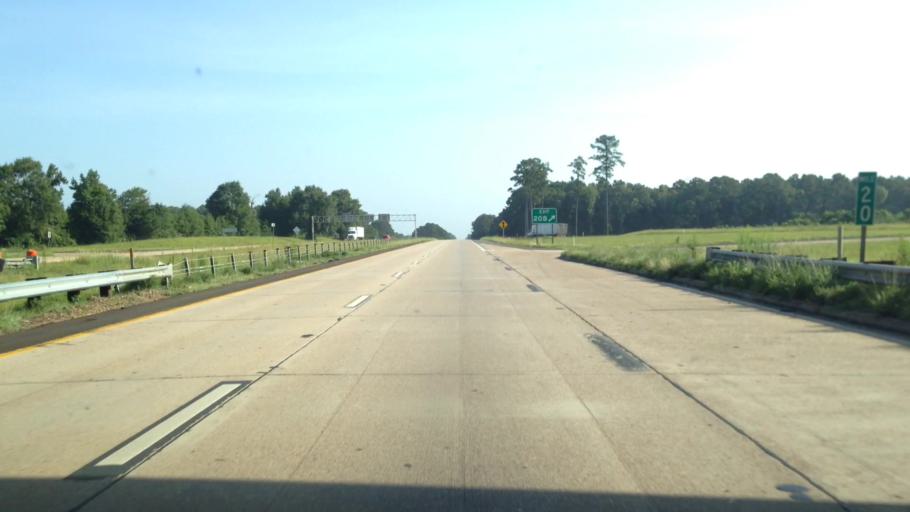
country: US
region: Mississippi
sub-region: Pike County
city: Summit
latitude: 31.2888
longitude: -90.4785
